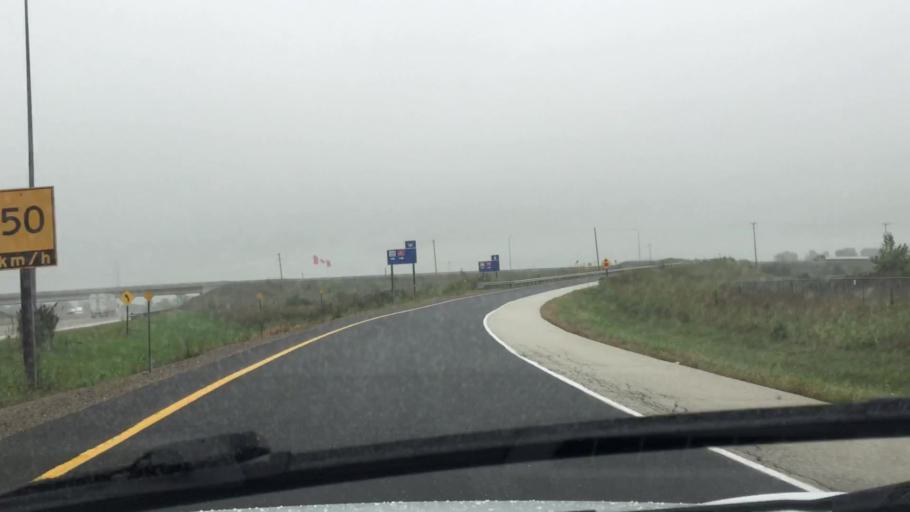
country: CA
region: Ontario
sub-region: Lambton County
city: Walpole Island
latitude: 42.2421
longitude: -82.5554
